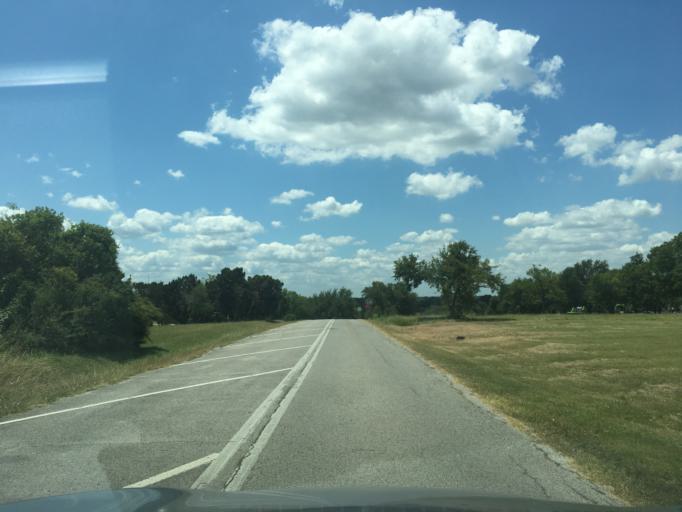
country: US
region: Texas
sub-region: Dallas County
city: Highland Park
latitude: 32.8633
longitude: -96.7228
